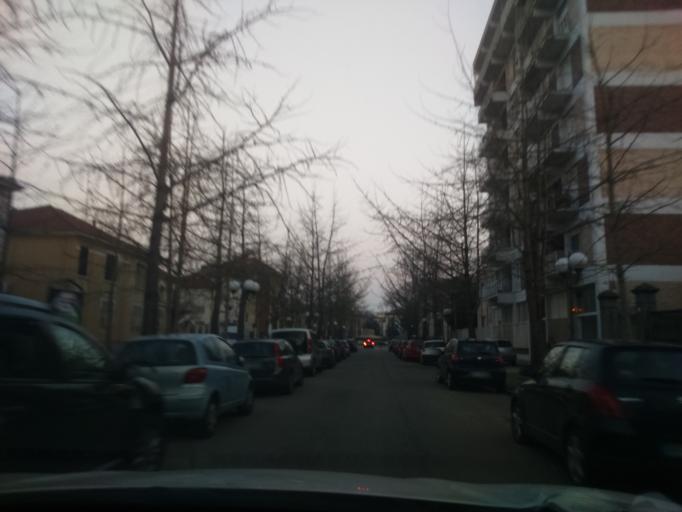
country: IT
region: Piedmont
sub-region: Provincia di Vercelli
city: Vercelli
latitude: 45.3215
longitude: 8.4169
